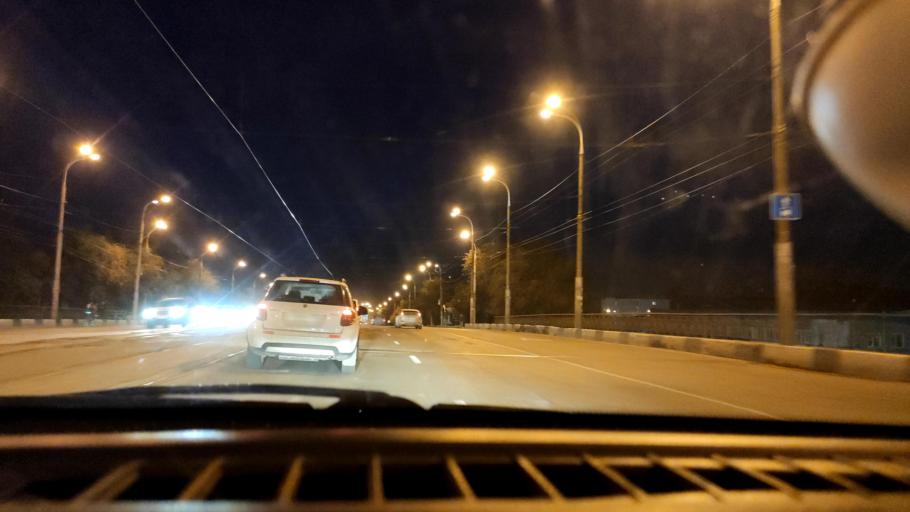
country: RU
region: Samara
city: Samara
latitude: 53.2131
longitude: 50.2703
